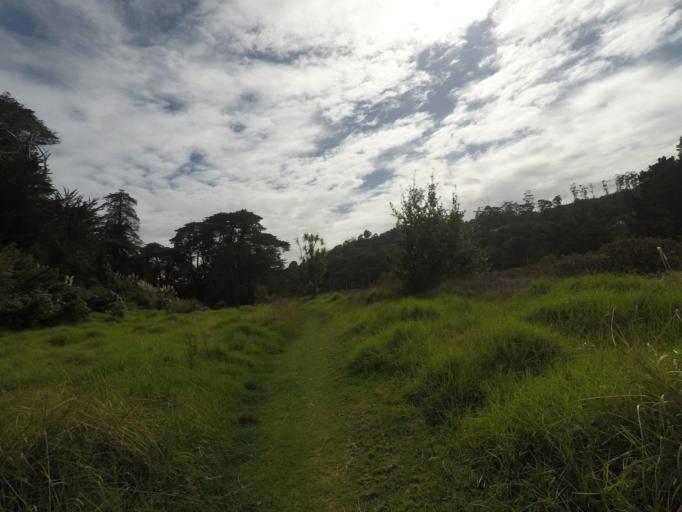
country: NZ
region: Auckland
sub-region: Auckland
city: Rothesay Bay
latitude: -36.6404
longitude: 174.7222
